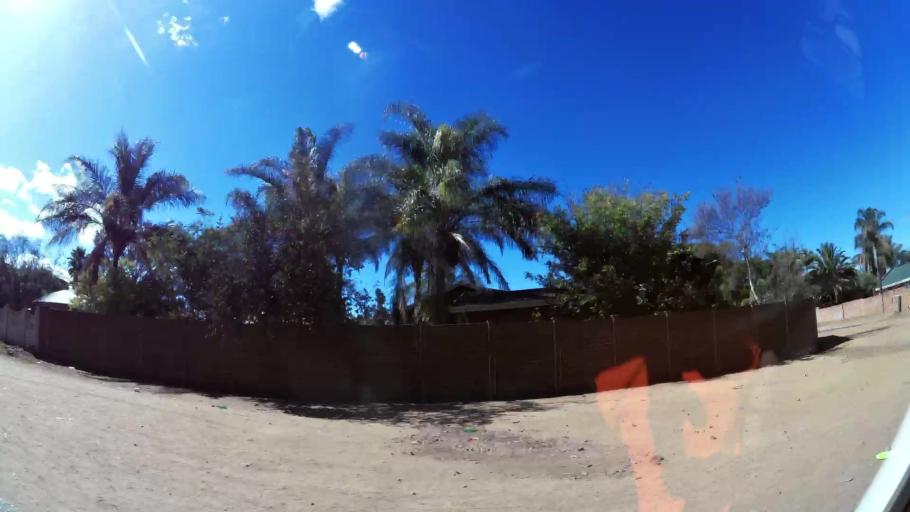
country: ZA
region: Limpopo
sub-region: Capricorn District Municipality
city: Polokwane
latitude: -23.9071
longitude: 29.4897
